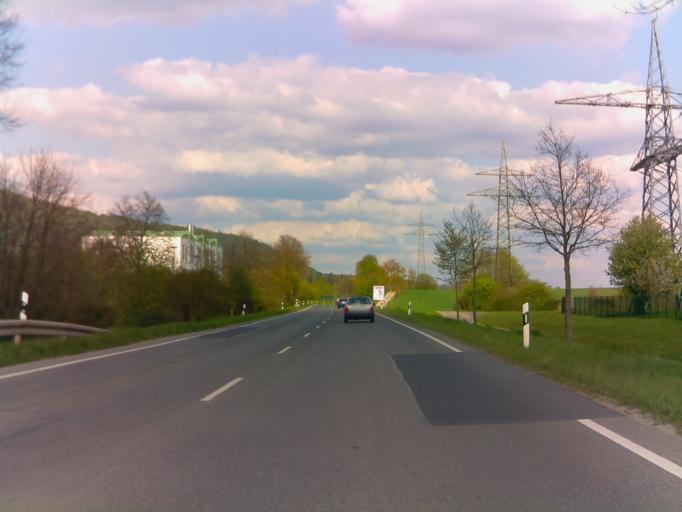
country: DE
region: Bavaria
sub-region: Upper Franconia
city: Neustadt bei Coburg
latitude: 50.3113
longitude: 11.1153
